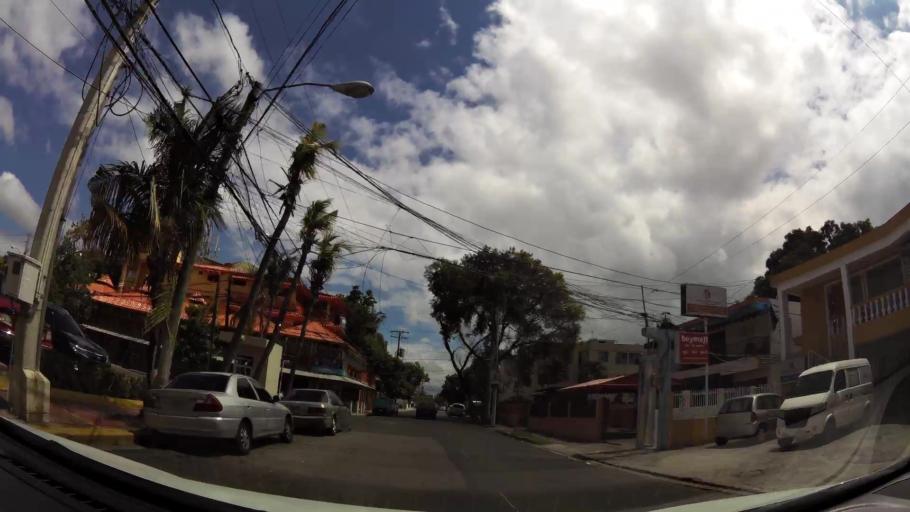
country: DO
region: Nacional
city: Bella Vista
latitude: 18.4574
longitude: -69.9554
